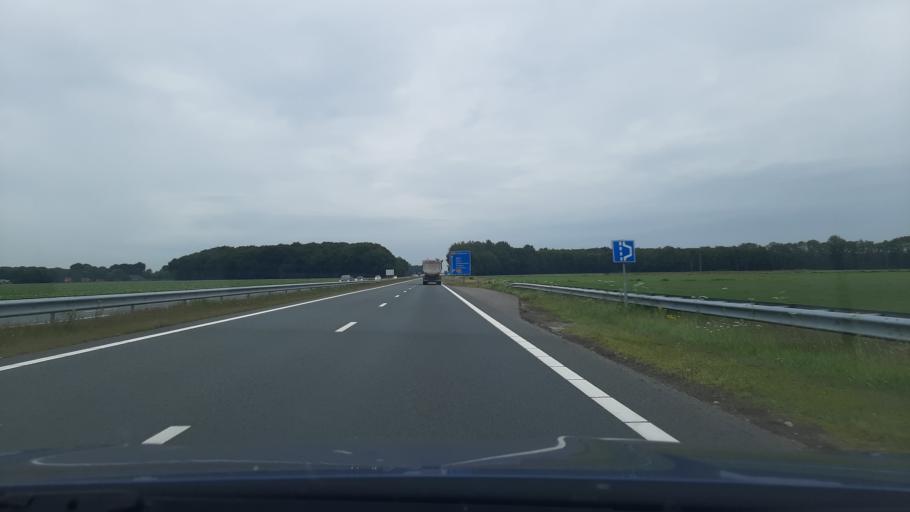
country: NL
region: Drenthe
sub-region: Gemeente Aa en Hunze
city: Anloo
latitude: 53.0069
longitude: 6.7328
